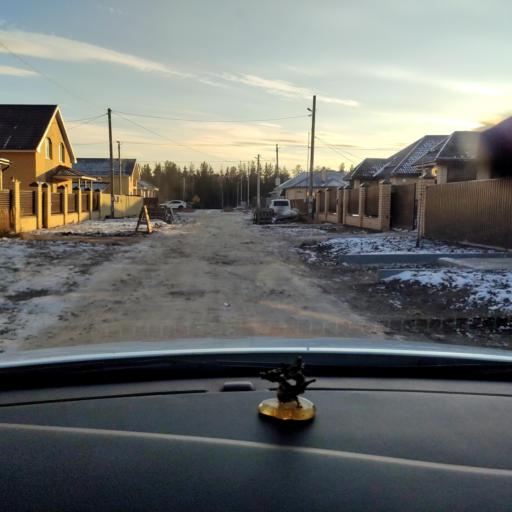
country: RU
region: Tatarstan
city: Stolbishchi
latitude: 55.6044
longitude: 49.1407
